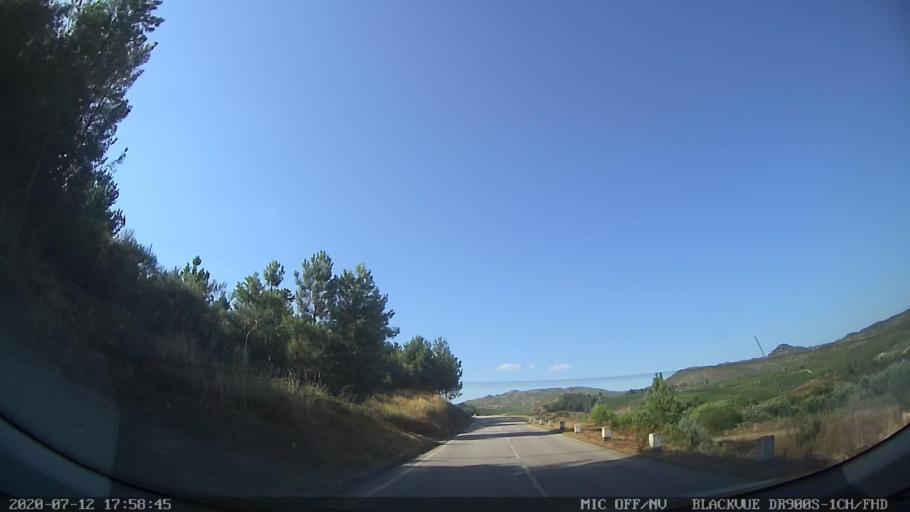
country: PT
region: Vila Real
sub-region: Sabrosa
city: Sabrosa
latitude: 41.2656
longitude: -7.4509
